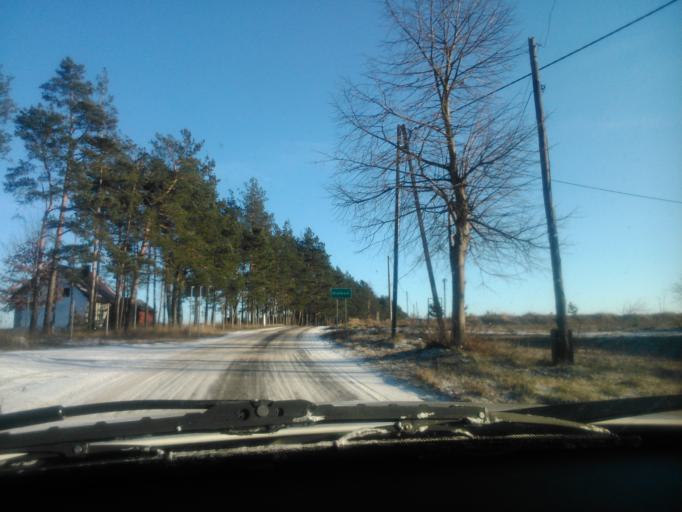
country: PL
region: Warmian-Masurian Voivodeship
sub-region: Powiat nowomiejski
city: Kurzetnik
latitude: 53.3712
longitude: 19.5294
